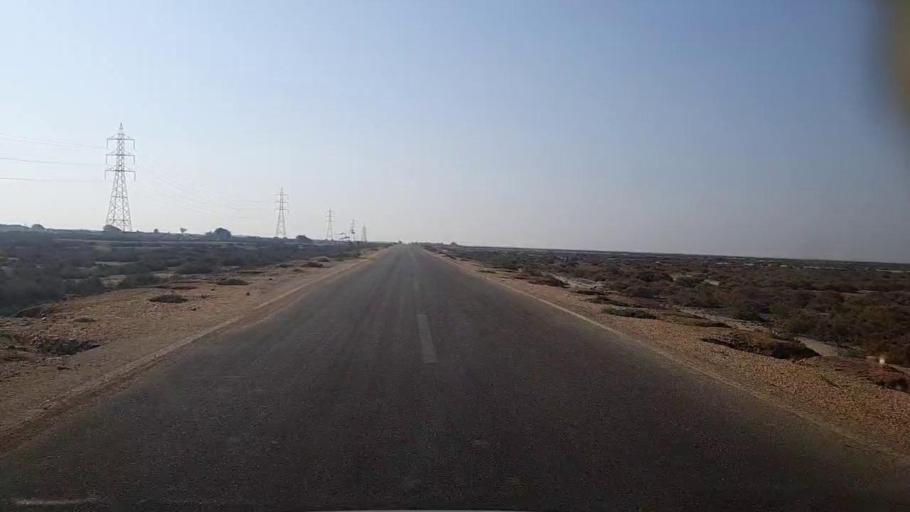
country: PK
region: Sindh
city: Gharo
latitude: 24.6240
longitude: 67.4969
